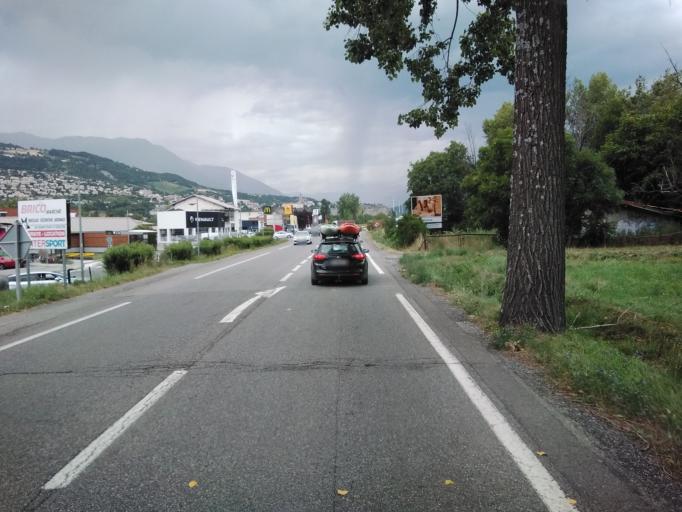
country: FR
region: Provence-Alpes-Cote d'Azur
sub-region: Departement des Hautes-Alpes
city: Embrun
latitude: 44.5464
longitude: 6.4823
